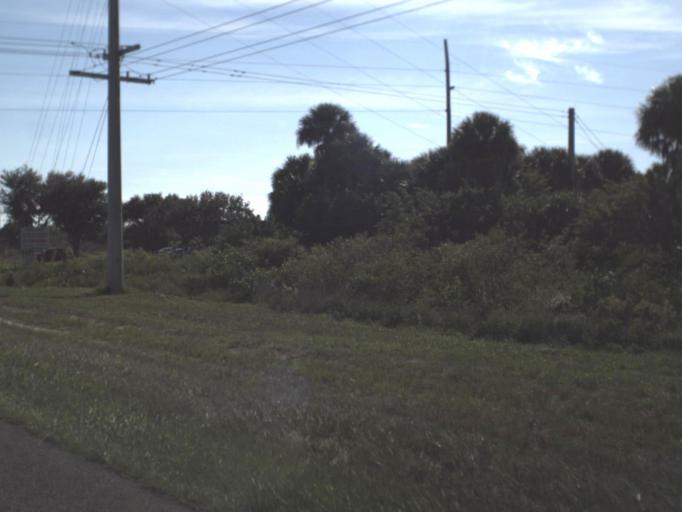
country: US
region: Florida
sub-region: Glades County
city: Moore Haven
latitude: 26.7689
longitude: -81.0831
